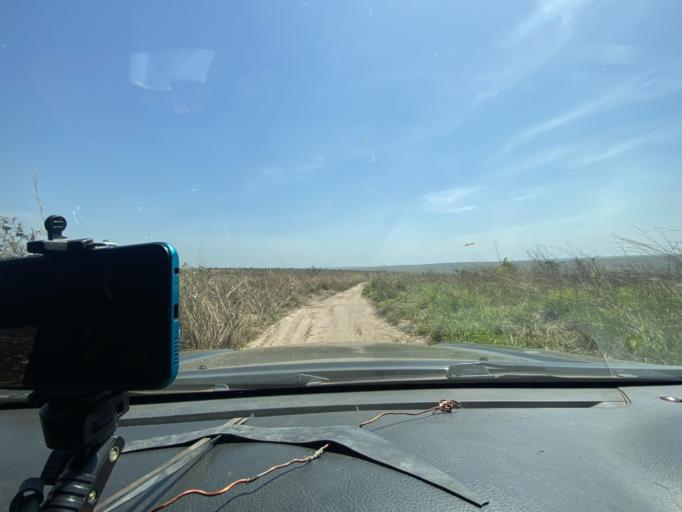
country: CD
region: Kasai-Oriental
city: Kabinda
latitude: -5.9439
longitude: 24.8067
